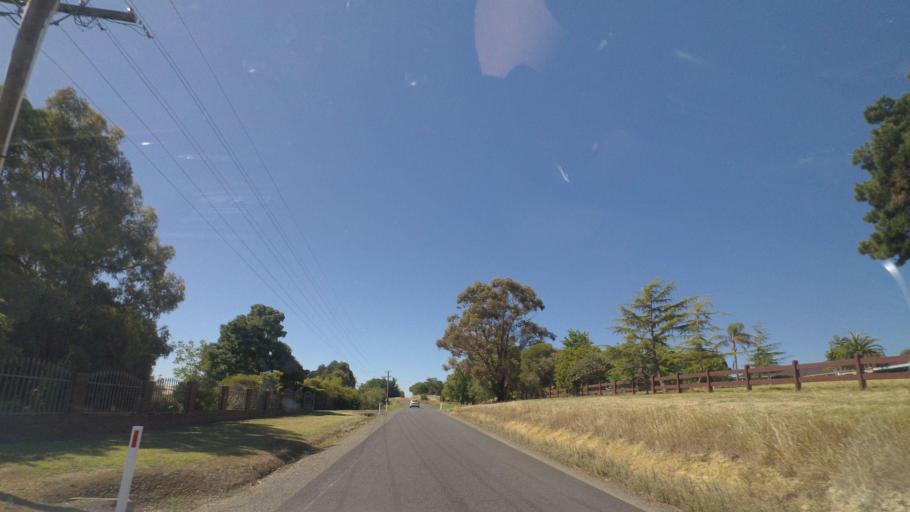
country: AU
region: Victoria
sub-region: Yarra Ranges
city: Chirnside Park
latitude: -37.7430
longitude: 145.3244
